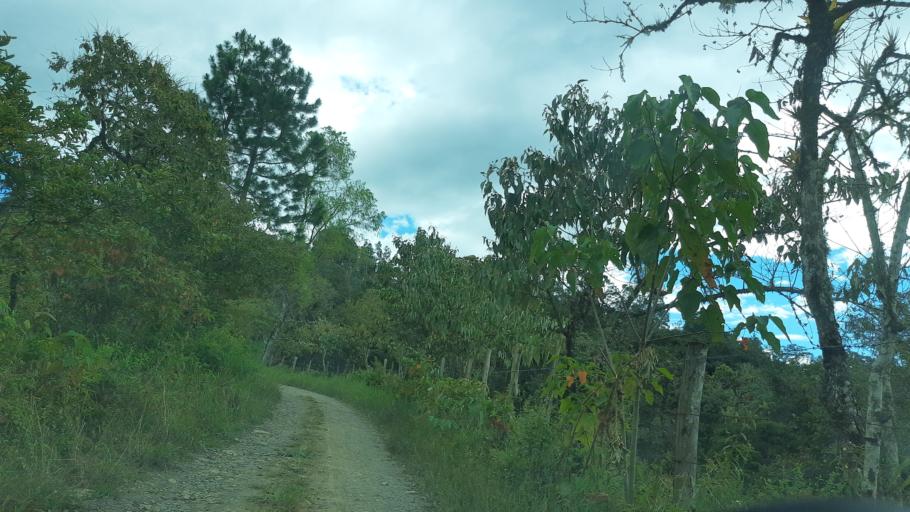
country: CO
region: Boyaca
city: Garagoa
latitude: 5.0365
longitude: -73.3311
